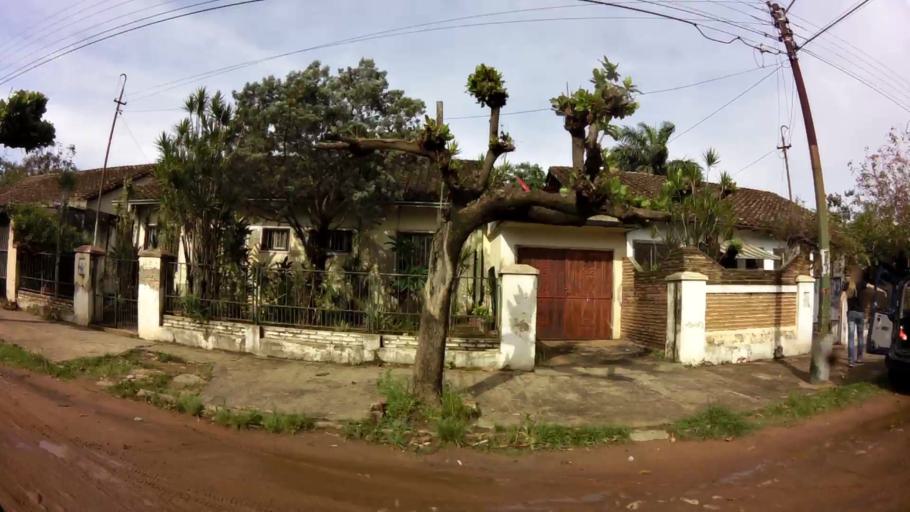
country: PY
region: Central
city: Limpio
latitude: -25.1787
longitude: -57.4920
